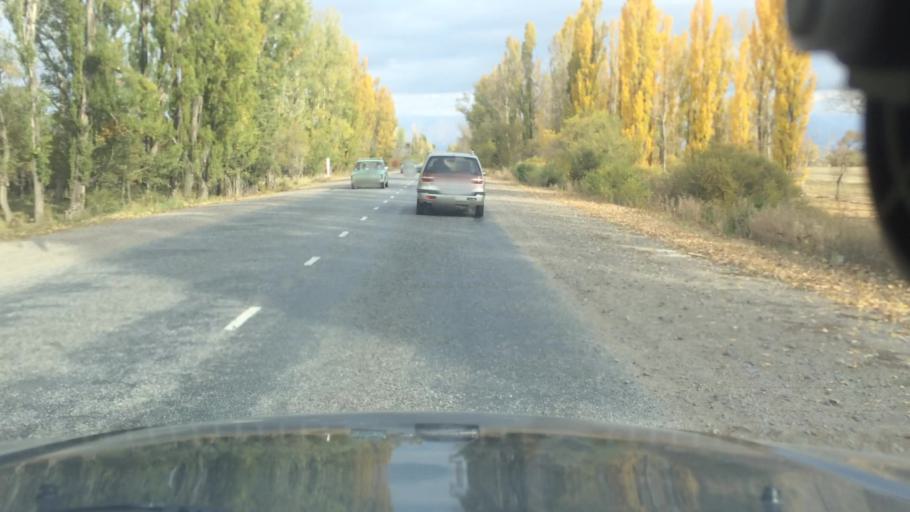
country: KG
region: Ysyk-Koel
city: Tyup
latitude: 42.6152
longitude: 78.3655
